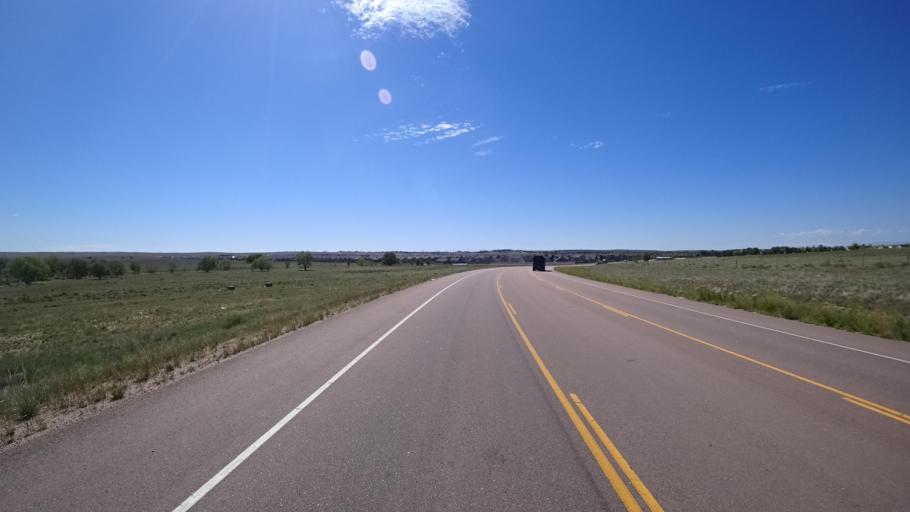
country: US
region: Colorado
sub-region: El Paso County
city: Security-Widefield
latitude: 38.7474
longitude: -104.6490
